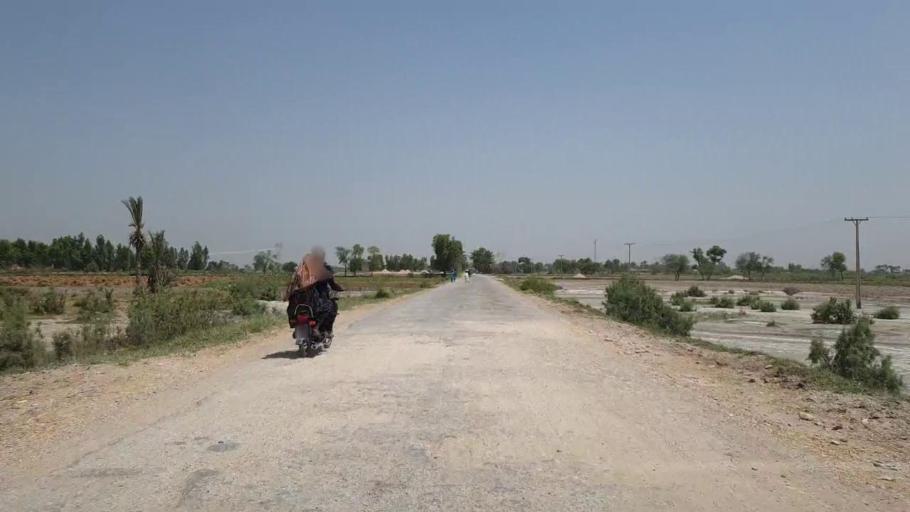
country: PK
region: Sindh
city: Adilpur
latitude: 27.8843
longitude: 69.2877
